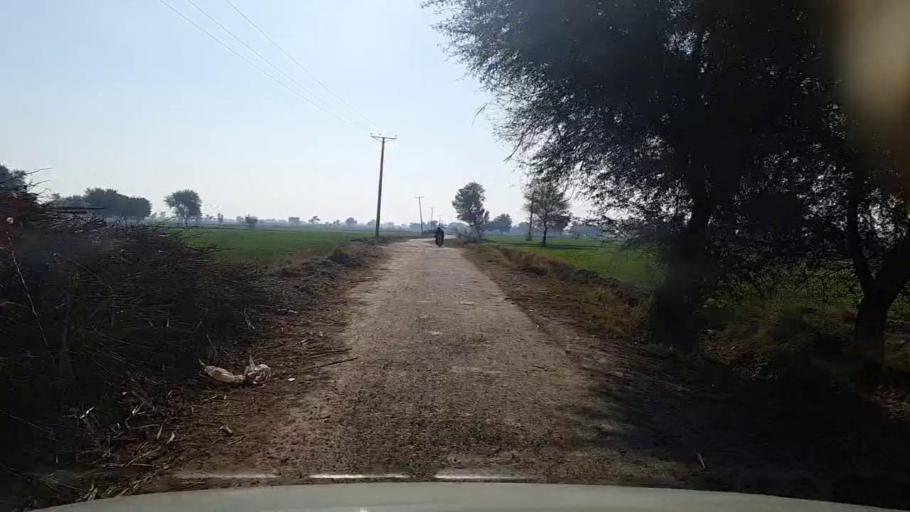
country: PK
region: Sindh
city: Khairpur
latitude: 28.0552
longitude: 69.7308
